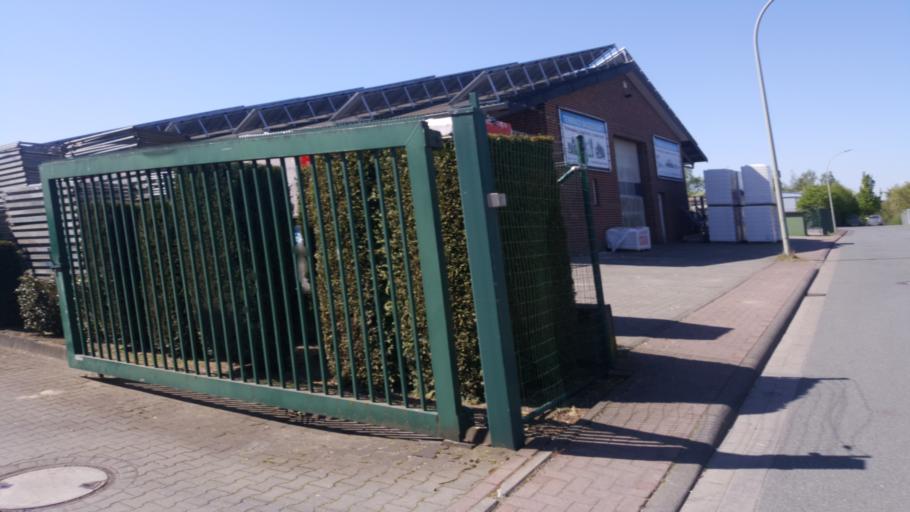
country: DE
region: North Rhine-Westphalia
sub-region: Regierungsbezirk Munster
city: Sudlohn
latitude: 51.9372
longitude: 6.8231
